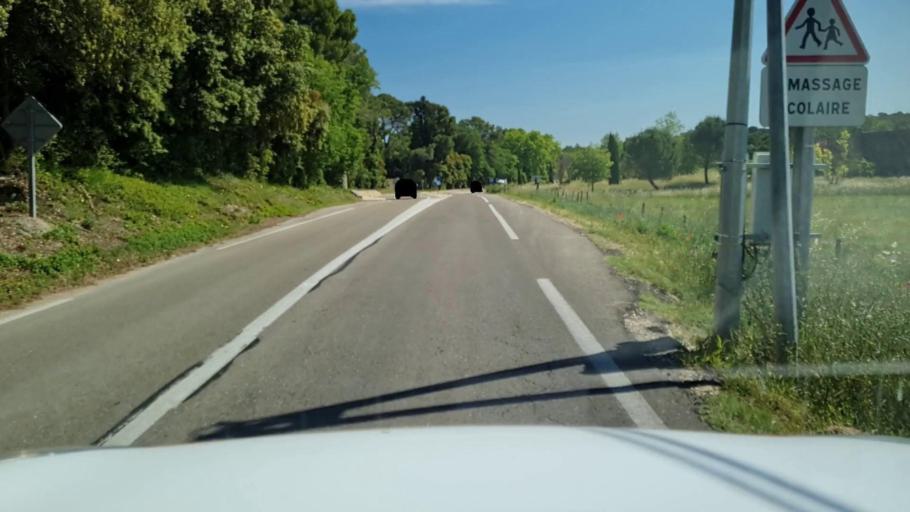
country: FR
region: Languedoc-Roussillon
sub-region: Departement du Gard
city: Villevieille
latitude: 43.8050
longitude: 4.0905
